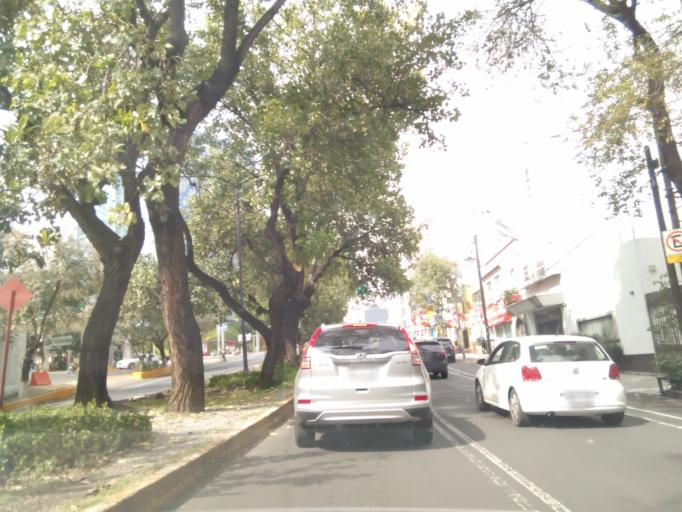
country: MX
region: Mexico City
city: Benito Juarez
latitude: 19.3989
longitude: -99.1700
